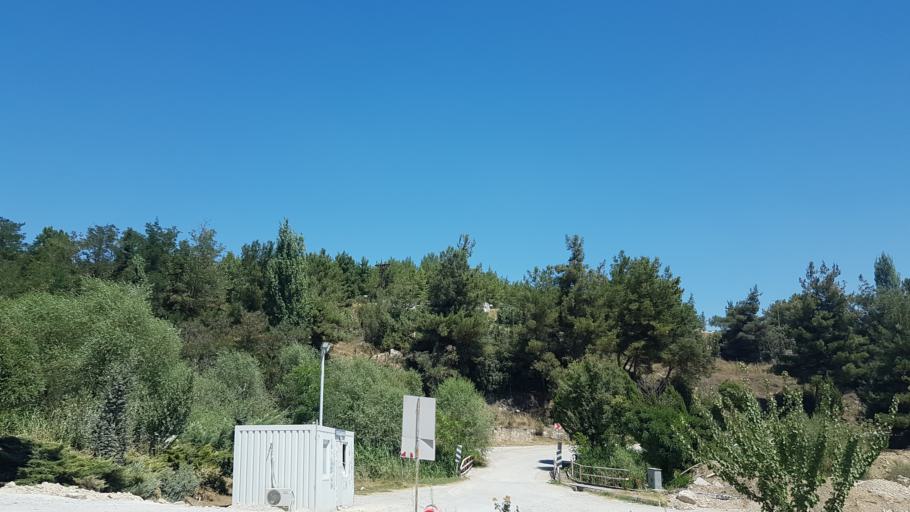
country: TR
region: Mugla
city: Yatagan
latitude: 37.3185
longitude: 28.0814
